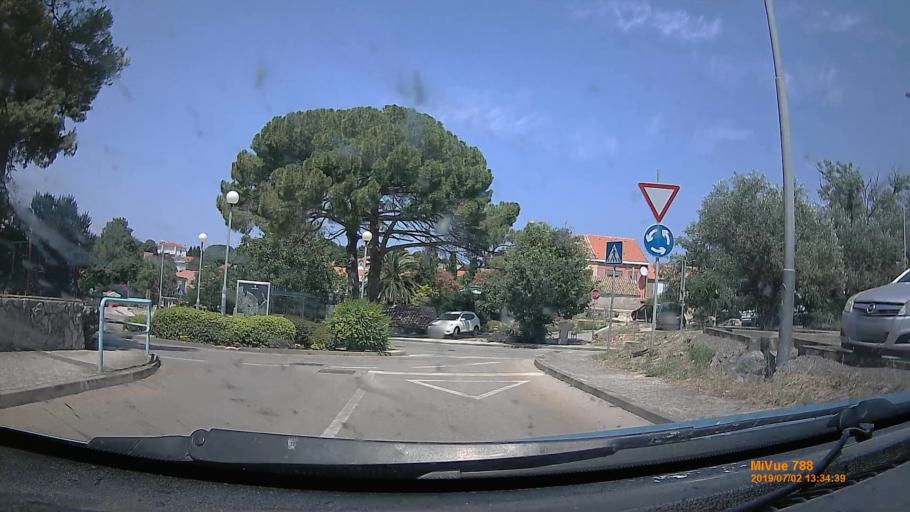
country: HR
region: Primorsko-Goranska
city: Mali Losinj
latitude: 44.5175
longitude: 14.5039
